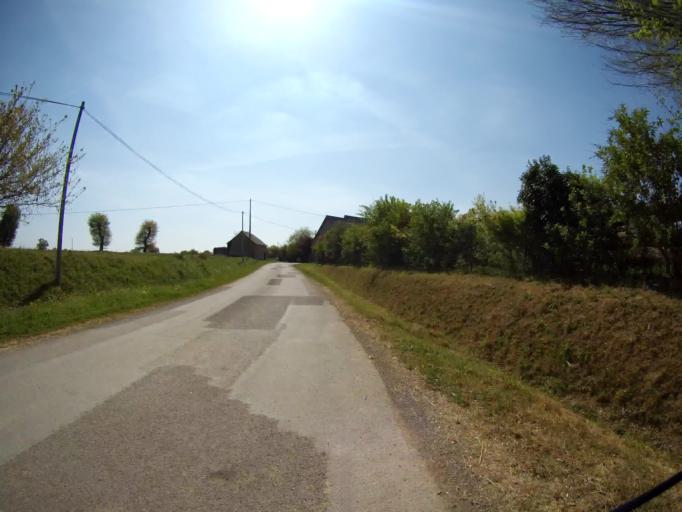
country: FR
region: Brittany
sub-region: Departement d'Ille-et-Vilaine
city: Vern-sur-Seiche
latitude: 48.0339
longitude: -1.6133
